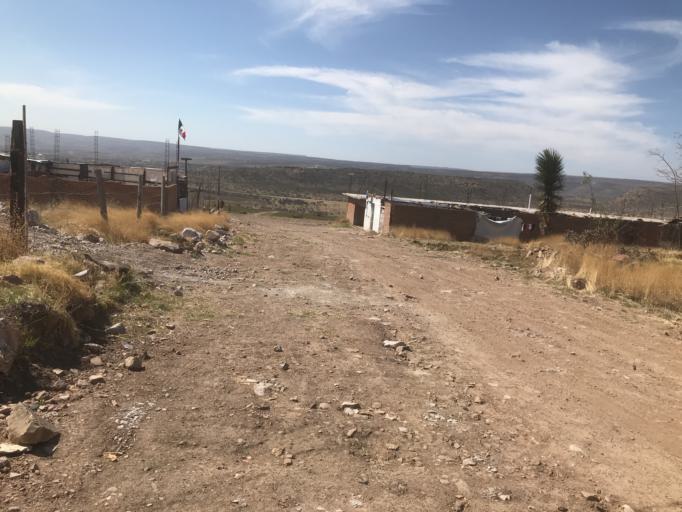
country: MX
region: Durango
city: Victoria de Durango
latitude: 24.0355
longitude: -104.7131
